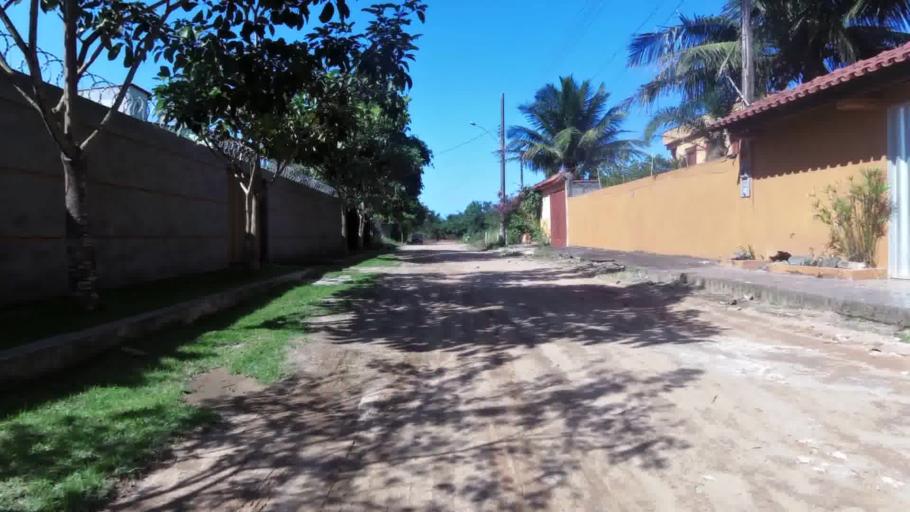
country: BR
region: Espirito Santo
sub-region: Piuma
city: Piuma
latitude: -20.8246
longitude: -40.6180
